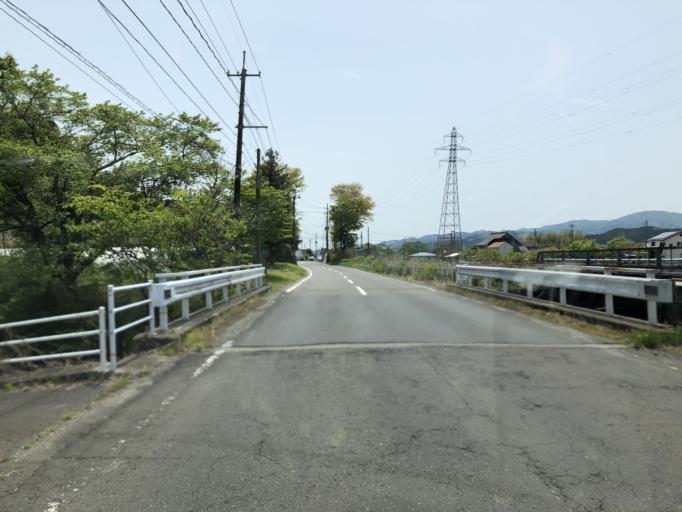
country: JP
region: Fukushima
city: Ishikawa
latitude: 37.0238
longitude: 140.3935
